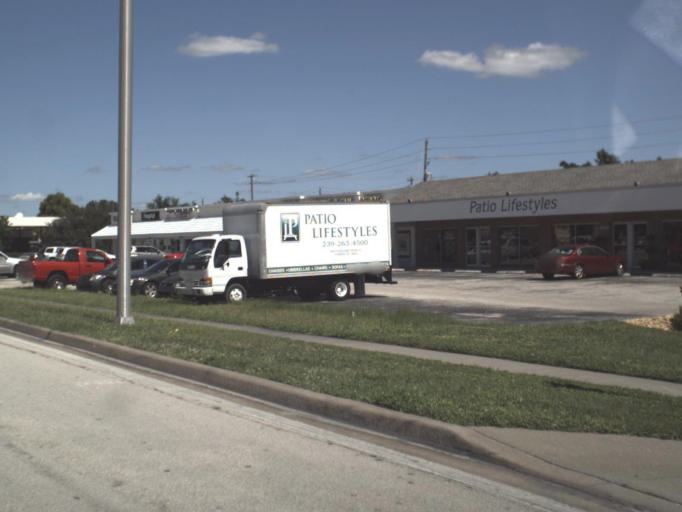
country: US
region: Florida
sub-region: Collier County
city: Pine Ridge
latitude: 26.2020
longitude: -81.8001
